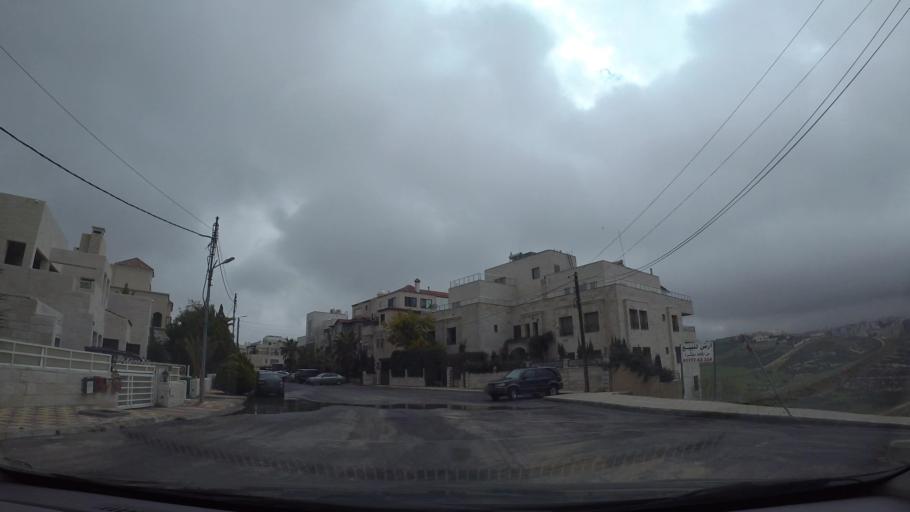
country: JO
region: Amman
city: Al Bunayyat ash Shamaliyah
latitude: 31.9345
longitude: 35.8885
